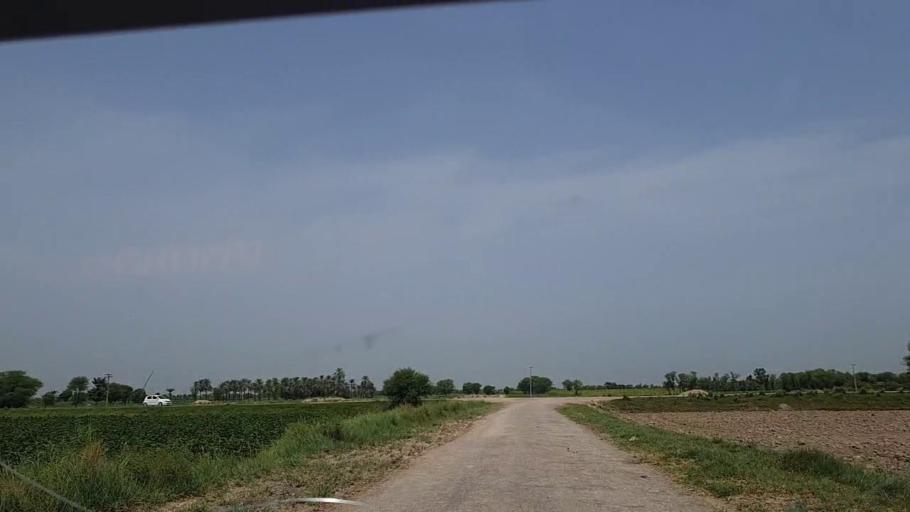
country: PK
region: Sindh
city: Tharu Shah
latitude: 26.9208
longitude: 68.0532
